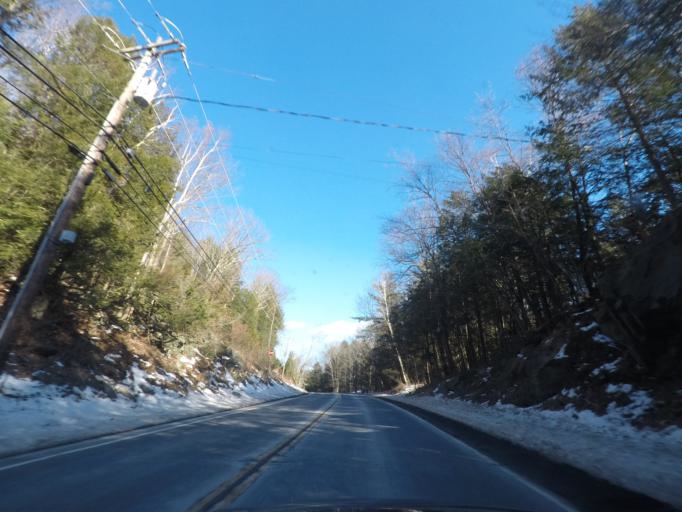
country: US
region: New York
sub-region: Columbia County
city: Chatham
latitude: 42.3192
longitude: -73.5159
